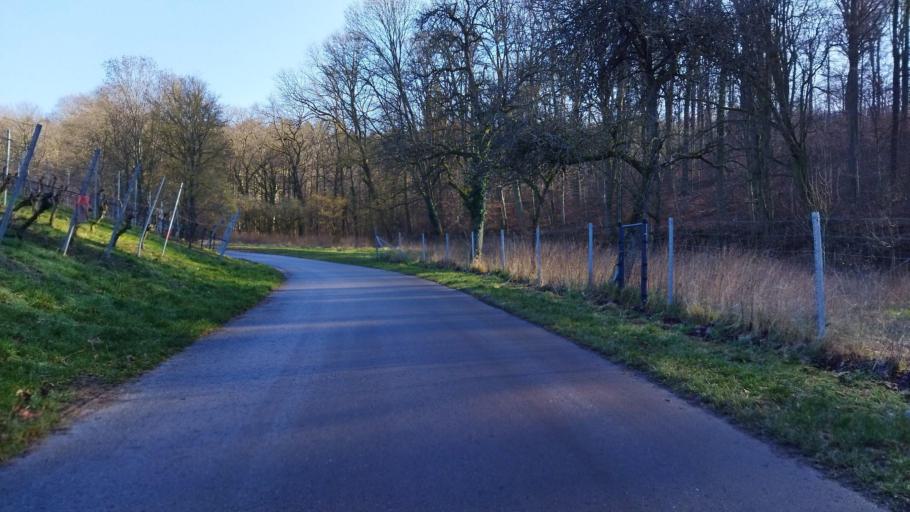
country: DE
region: Baden-Wuerttemberg
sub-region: Regierungsbezirk Stuttgart
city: Schwaigern
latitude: 49.1256
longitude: 9.0766
